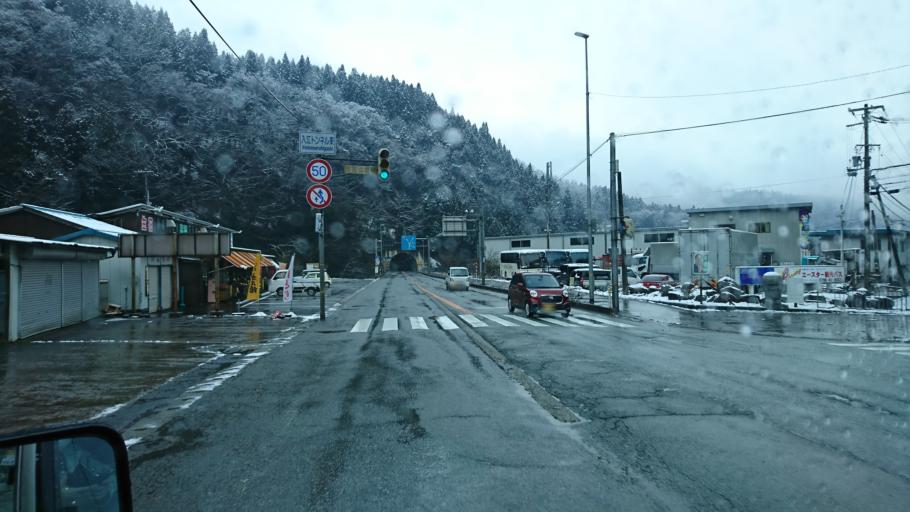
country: JP
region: Hyogo
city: Toyooka
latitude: 35.4902
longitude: 134.5697
